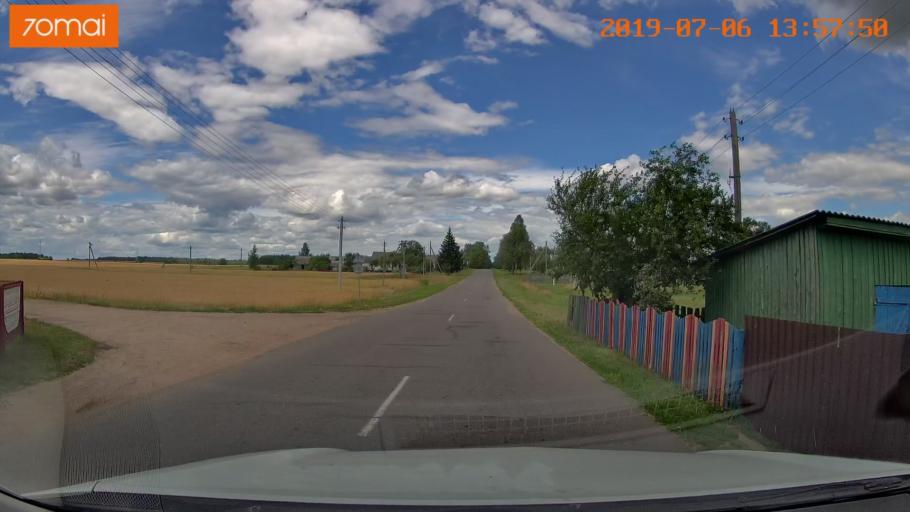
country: BY
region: Minsk
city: Ivyanyets
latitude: 53.7777
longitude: 26.8072
